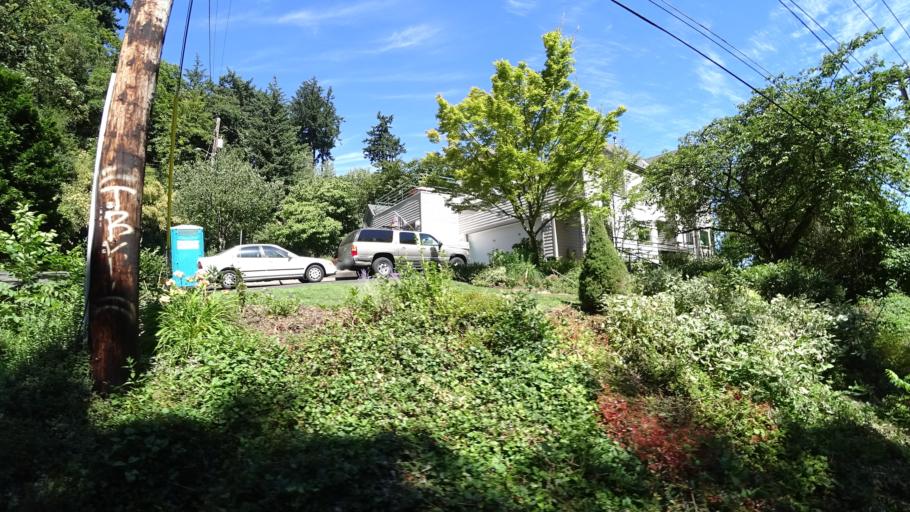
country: US
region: Oregon
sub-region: Multnomah County
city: Portland
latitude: 45.5134
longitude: -122.6948
